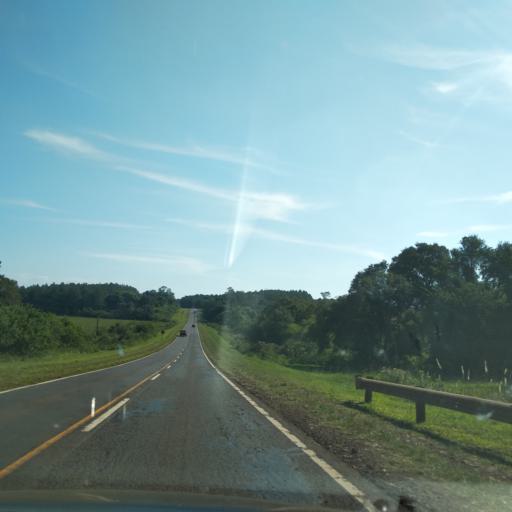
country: AR
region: Misiones
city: Santo Pipo
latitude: -27.1136
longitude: -55.3556
